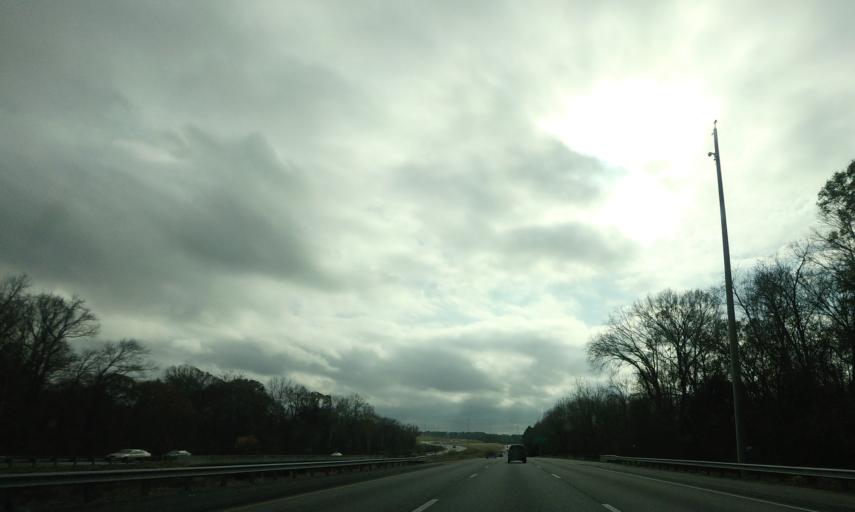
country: US
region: Georgia
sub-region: Bibb County
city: West Point
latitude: 32.7662
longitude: -83.7109
